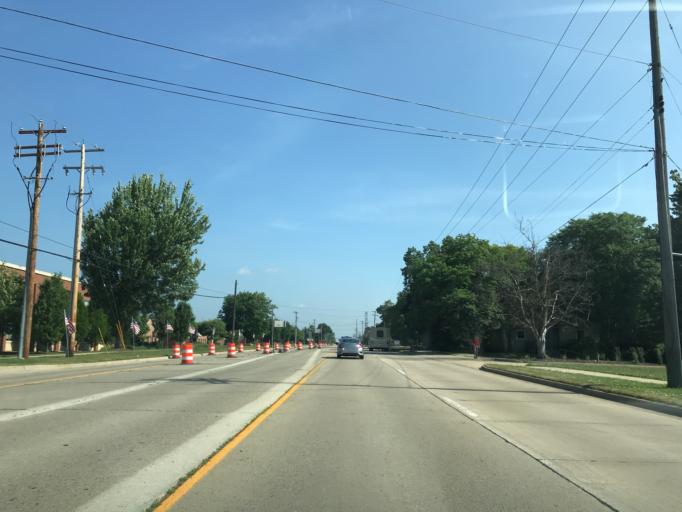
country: US
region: Michigan
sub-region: Ingham County
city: Okemos
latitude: 42.6862
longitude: -84.4324
